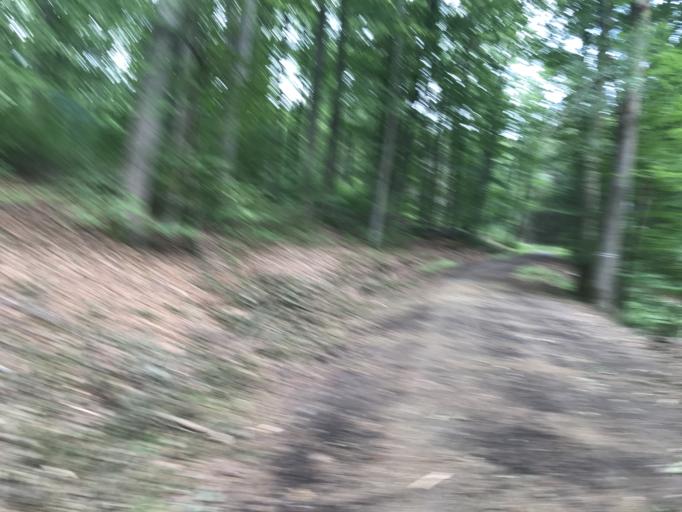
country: DE
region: Hesse
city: Lollar
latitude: 50.6509
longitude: 8.6389
